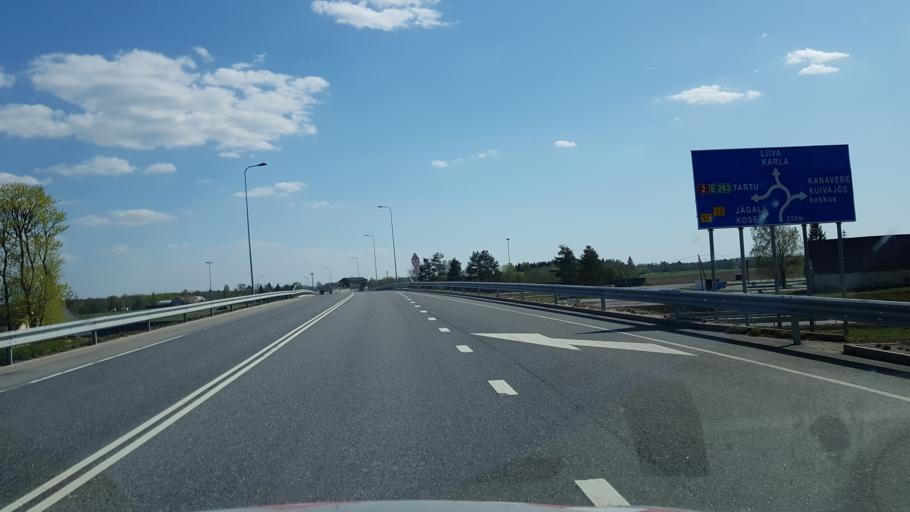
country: EE
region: Harju
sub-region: Rae vald
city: Vaida
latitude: 59.1844
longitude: 25.1164
